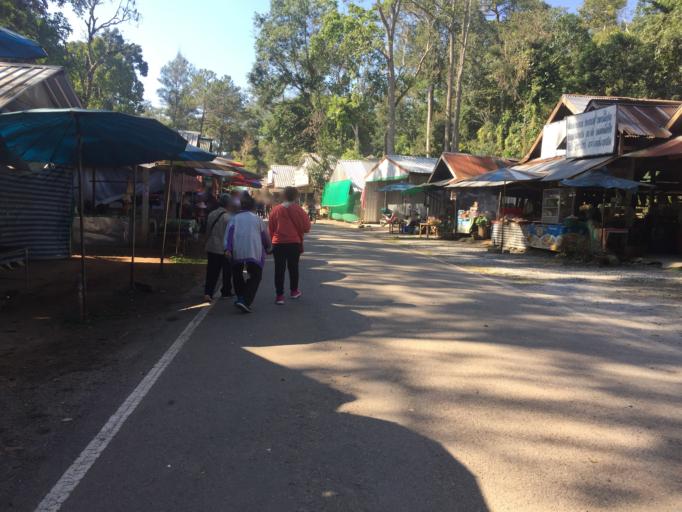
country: TH
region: Phetchabun
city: Khao Kho
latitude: 16.6285
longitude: 100.9401
